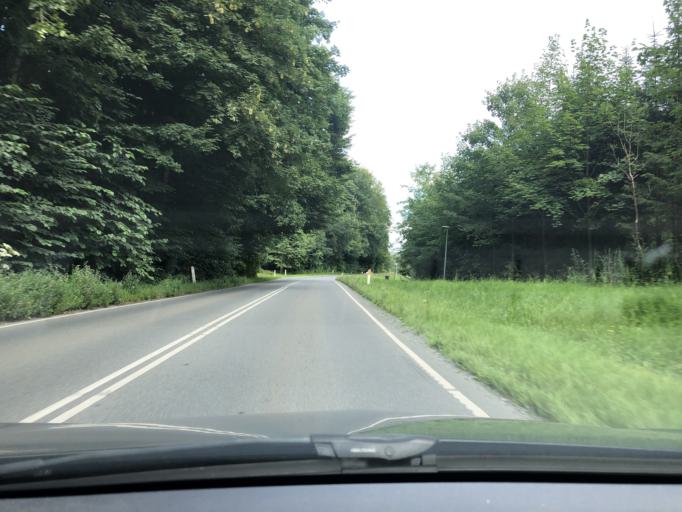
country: DK
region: South Denmark
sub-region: Vejle Kommune
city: Vejle
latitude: 55.6947
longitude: 9.4856
